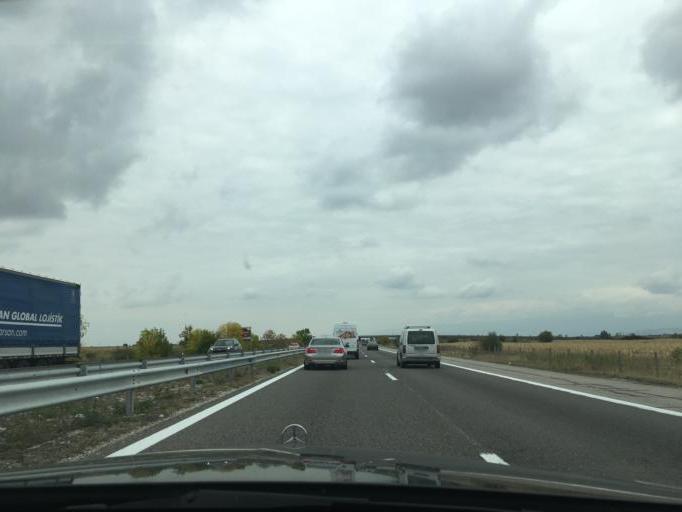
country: BG
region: Pazardzhik
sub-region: Obshtina Pazardzhik
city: Pazardzhik
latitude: 42.2478
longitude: 24.3500
